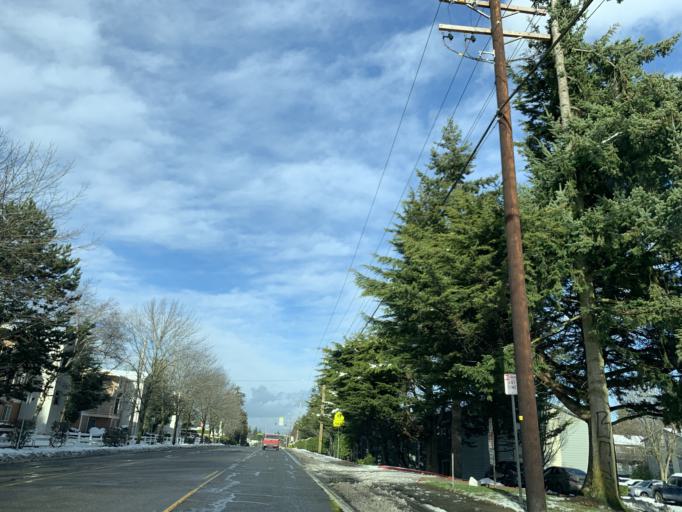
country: US
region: Washington
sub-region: Snohomish County
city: Martha Lake
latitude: 47.9184
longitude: -122.2404
